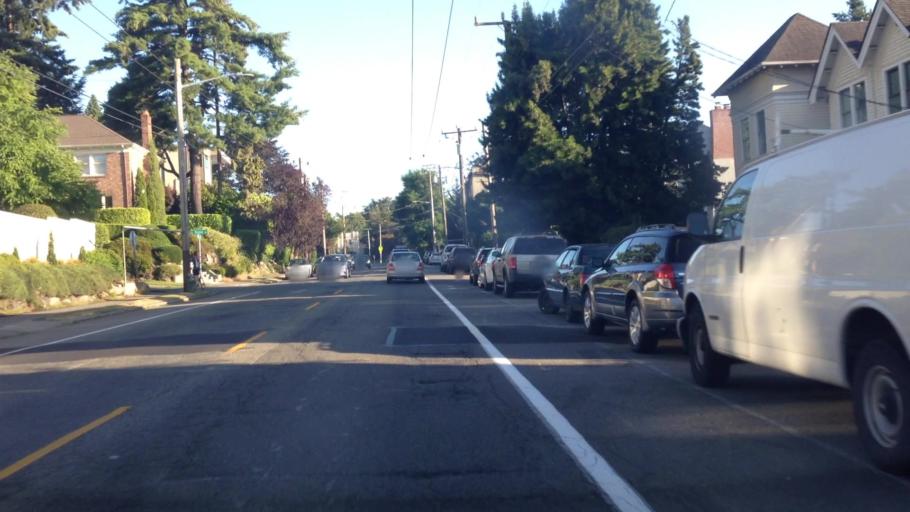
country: US
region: Washington
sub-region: King County
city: Seattle
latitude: 47.6355
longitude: -122.3201
